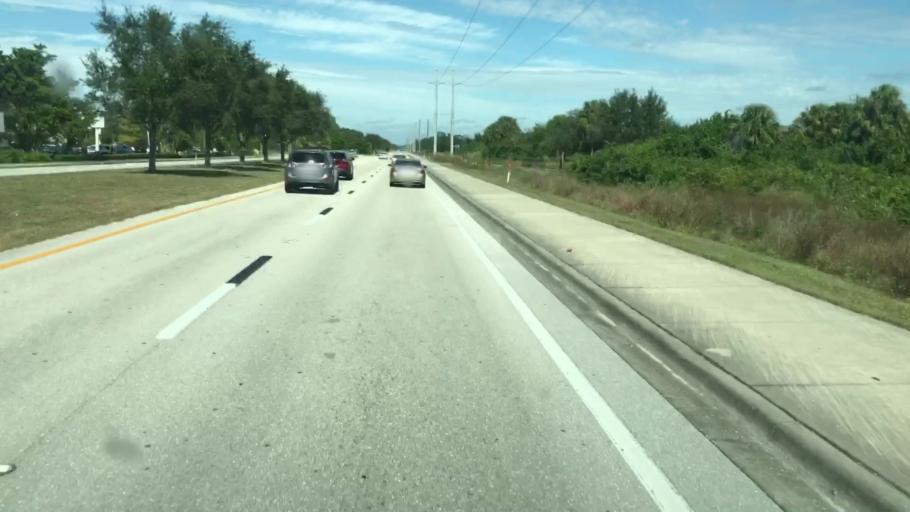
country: US
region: Florida
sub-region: Lee County
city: Gateway
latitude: 26.5964
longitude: -81.7127
